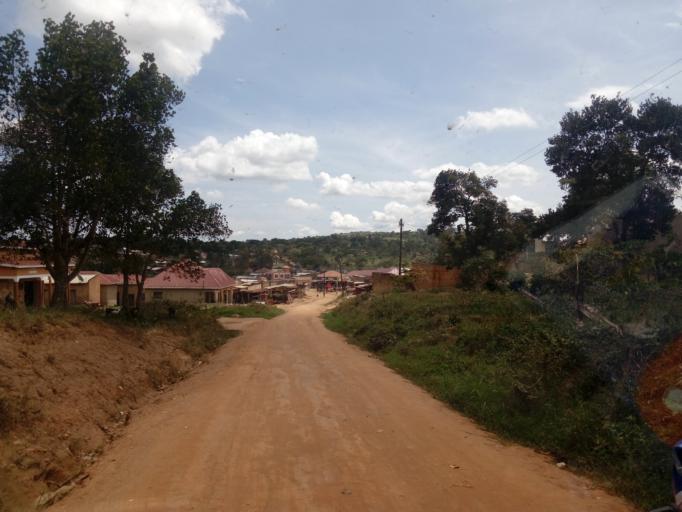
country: UG
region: Central Region
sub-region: Mubende District
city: Mubende
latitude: 0.4489
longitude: 31.6896
